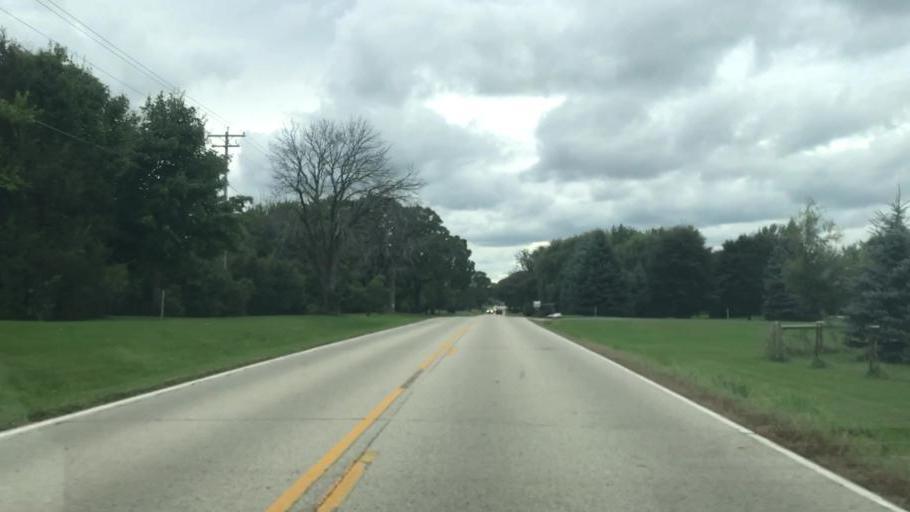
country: US
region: Wisconsin
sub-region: Waukesha County
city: Mukwonago
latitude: 42.8824
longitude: -88.3678
